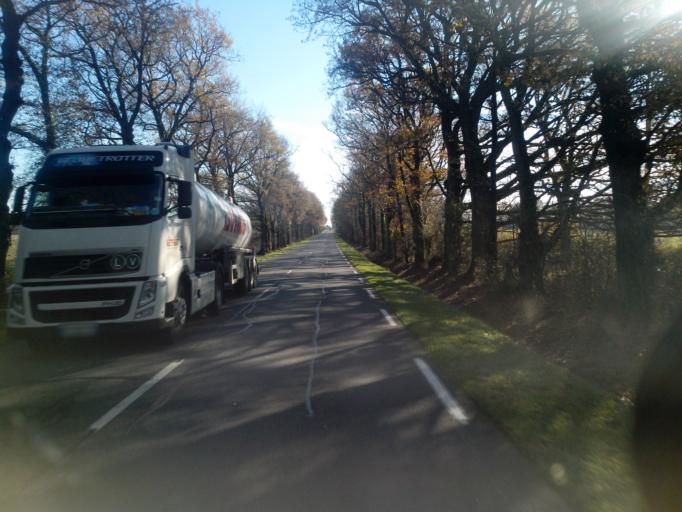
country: FR
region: Limousin
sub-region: Departement de la Haute-Vienne
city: Bussiere-Poitevine
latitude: 46.2490
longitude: 0.8841
